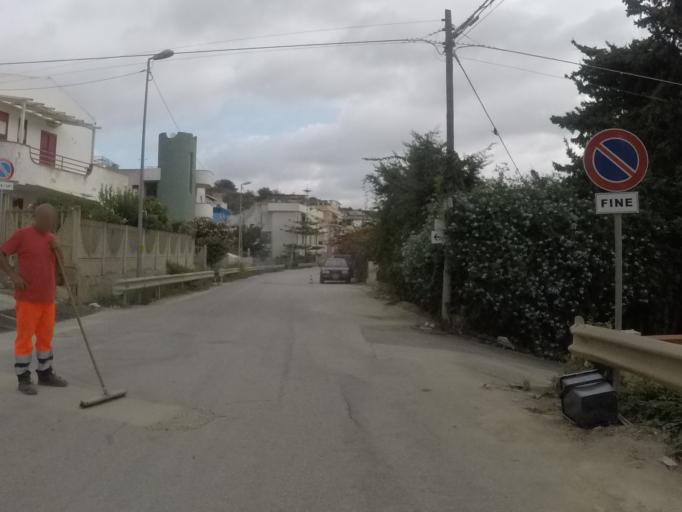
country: IT
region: Sicily
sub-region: Agrigento
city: Realmonte
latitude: 37.2896
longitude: 13.4824
